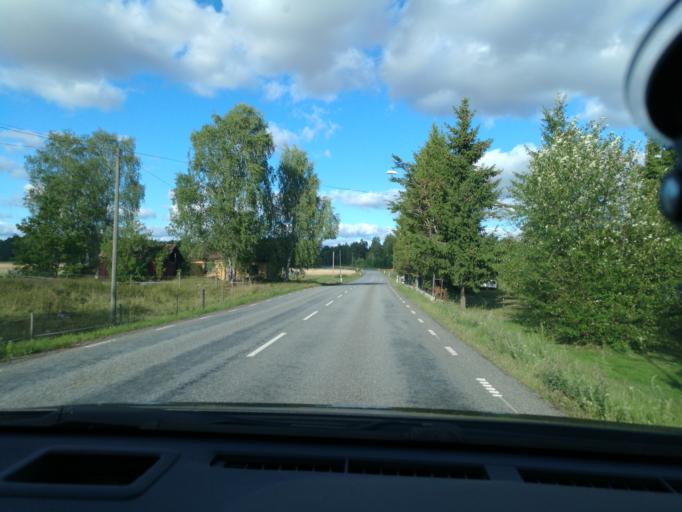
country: SE
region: Vaestmanland
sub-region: Hallstahammars Kommun
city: Kolback
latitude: 59.5377
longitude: 16.1505
